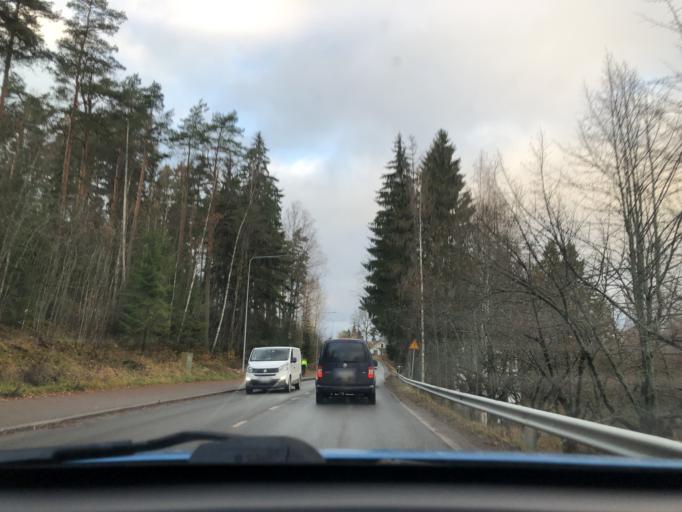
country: FI
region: Pirkanmaa
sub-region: Tampere
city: Kangasala
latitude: 61.4660
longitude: 24.0676
